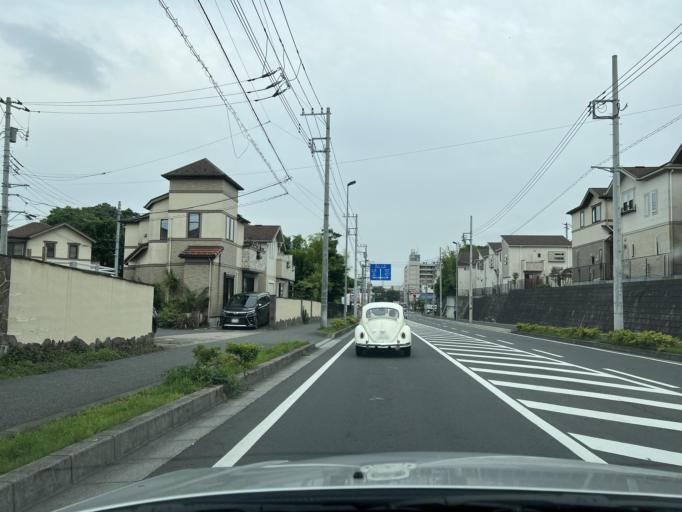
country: JP
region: Chiba
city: Nagareyama
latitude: 35.8222
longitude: 139.9292
